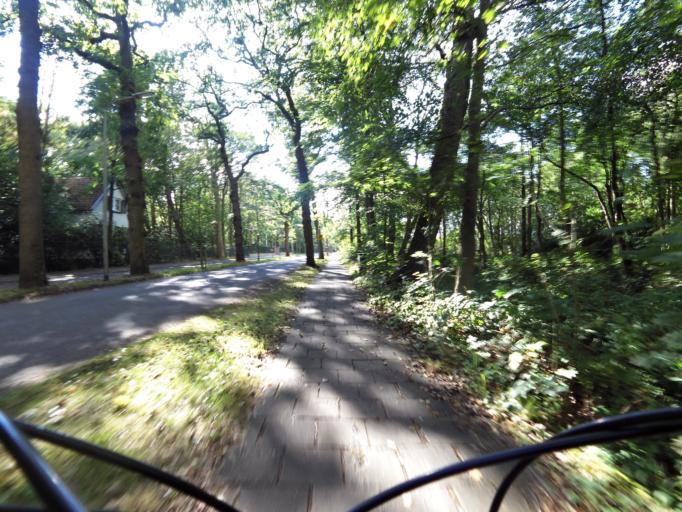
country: NL
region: South Holland
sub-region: Gemeente Leidschendam-Voorburg
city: Voorburg
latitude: 52.1176
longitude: 4.3542
